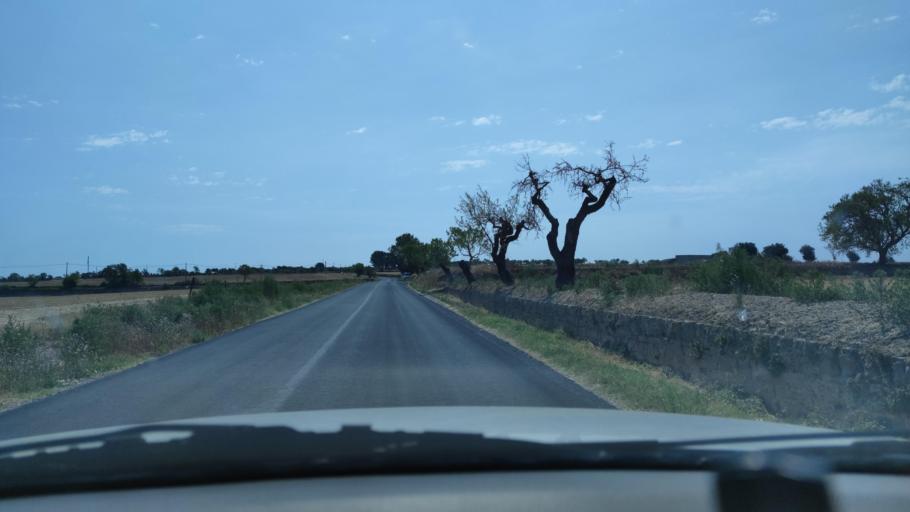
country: ES
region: Catalonia
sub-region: Provincia de Lleida
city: Ivorra
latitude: 41.7830
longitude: 1.2981
